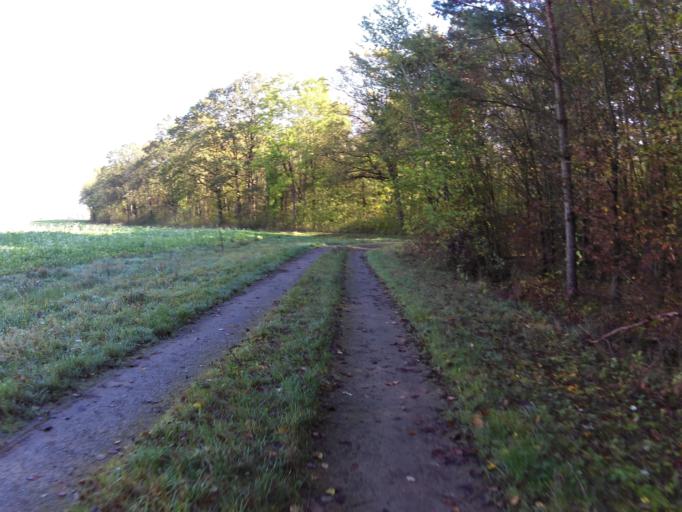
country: DE
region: Bavaria
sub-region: Regierungsbezirk Unterfranken
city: Biebelried
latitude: 49.7226
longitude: 10.0889
